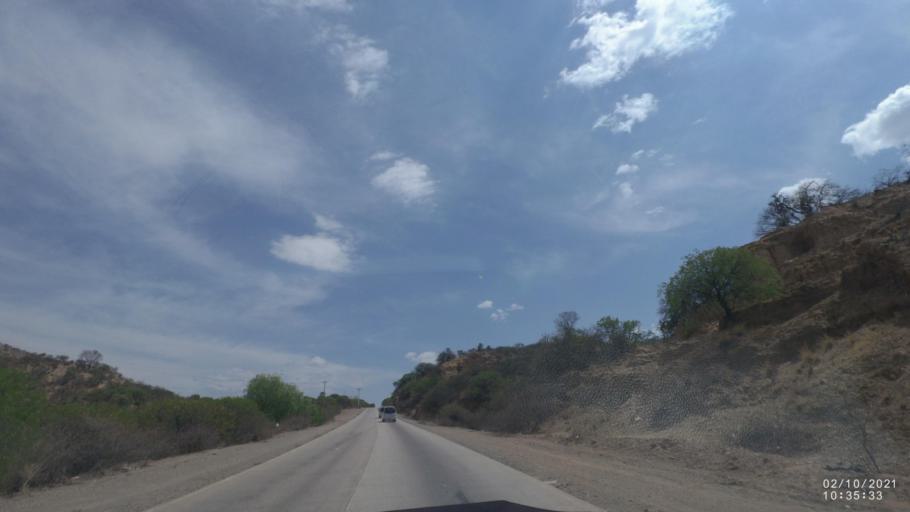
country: BO
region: Cochabamba
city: Capinota
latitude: -17.6597
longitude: -66.2576
